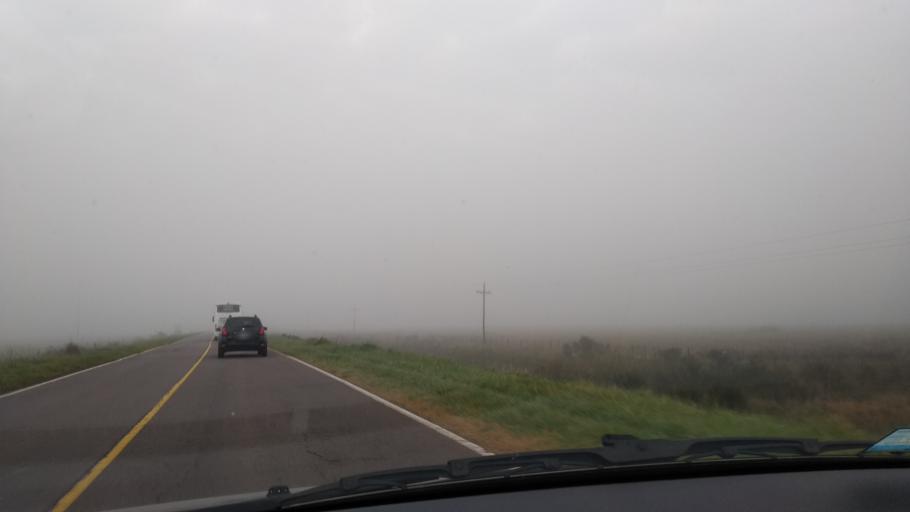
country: AR
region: Buenos Aires
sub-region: Partido de San Vicente
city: San Vicente
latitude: -35.2695
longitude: -58.5349
